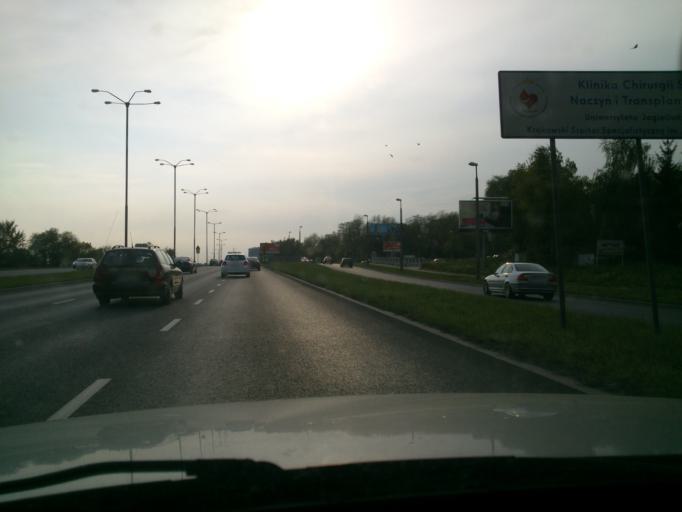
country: PL
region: Lesser Poland Voivodeship
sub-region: Krakow
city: Krakow
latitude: 50.0876
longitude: 19.9973
